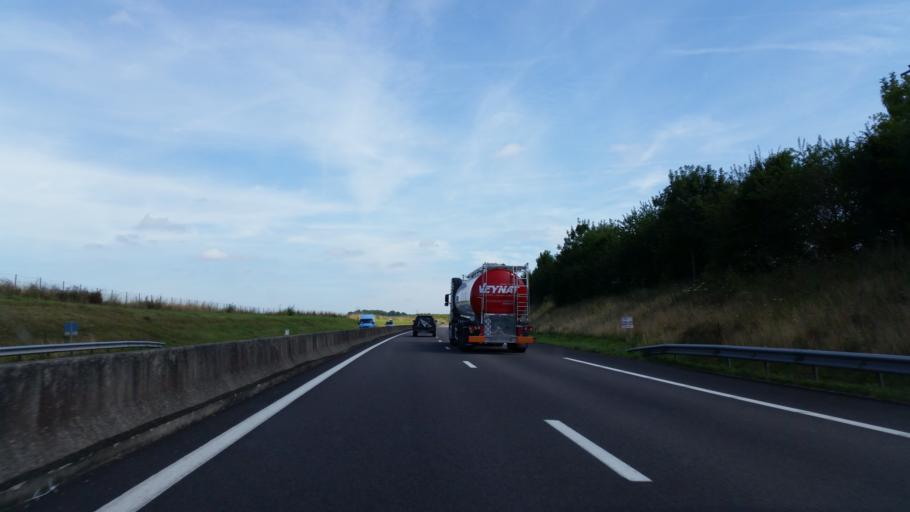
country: FR
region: Haute-Normandie
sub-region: Departement de la Seine-Maritime
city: Aumale
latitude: 49.7707
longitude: 1.7131
